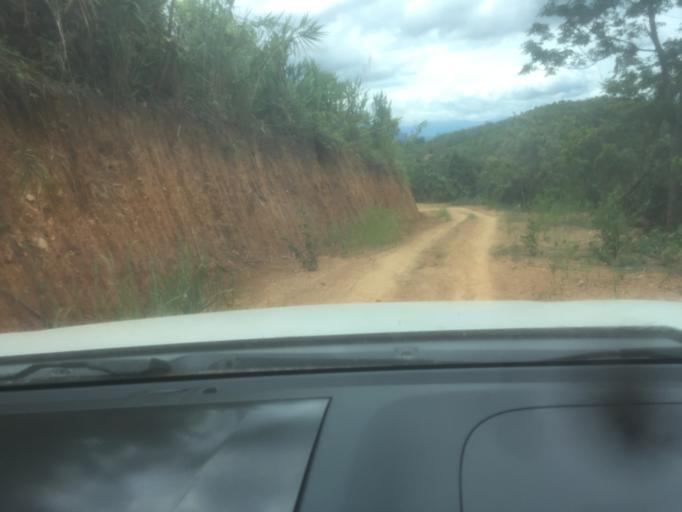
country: LA
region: Phongsali
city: Khoa
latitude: 20.9269
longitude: 102.5383
